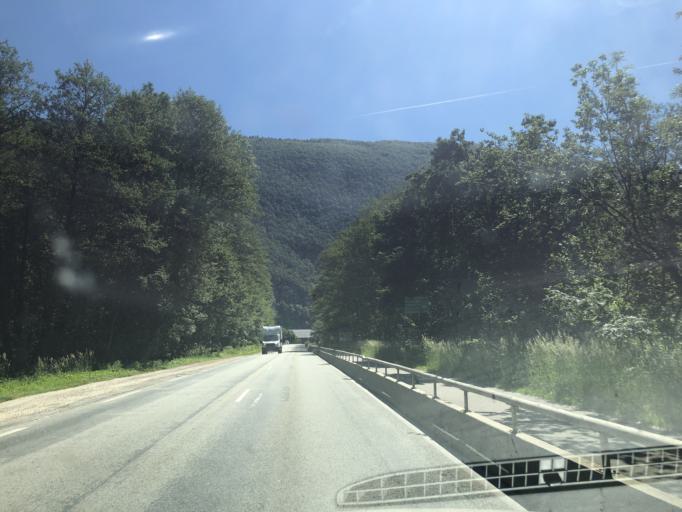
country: FR
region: Rhone-Alpes
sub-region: Departement de la Savoie
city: Novalaise
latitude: 45.5737
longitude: 5.7961
